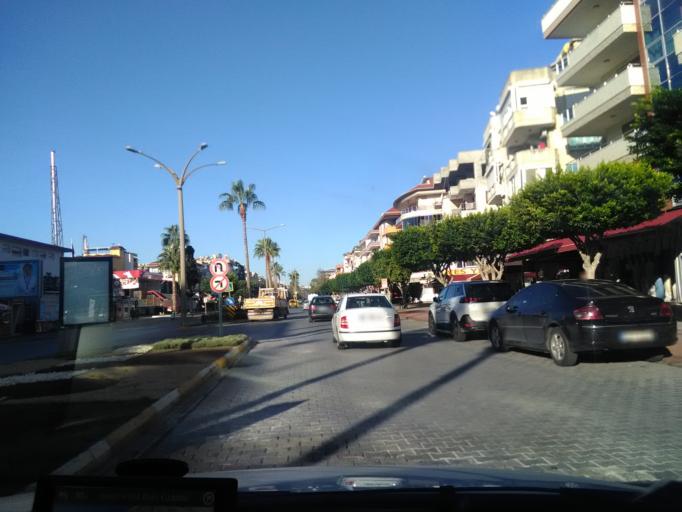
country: TR
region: Antalya
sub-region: Alanya
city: Alanya
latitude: 36.5461
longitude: 31.9902
